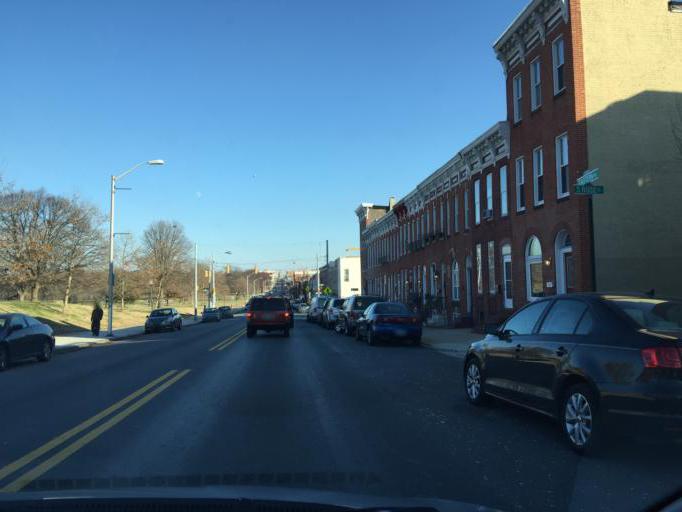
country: US
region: Maryland
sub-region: City of Baltimore
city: Baltimore
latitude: 39.2861
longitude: -76.5809
